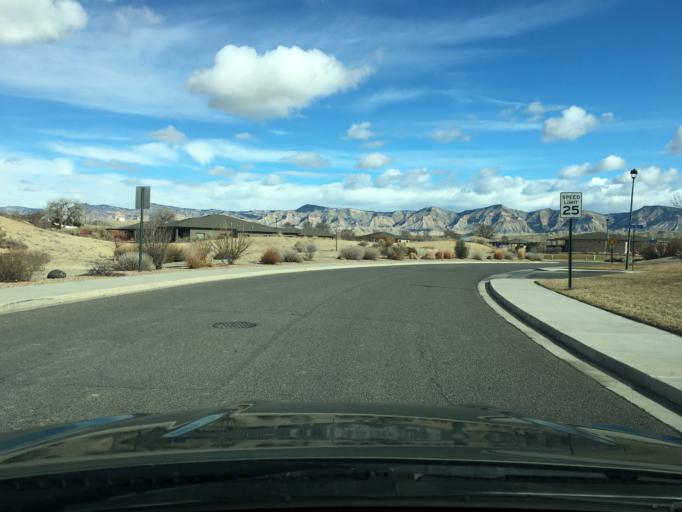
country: US
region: Colorado
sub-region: Mesa County
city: Grand Junction
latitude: 39.1301
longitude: -108.5566
